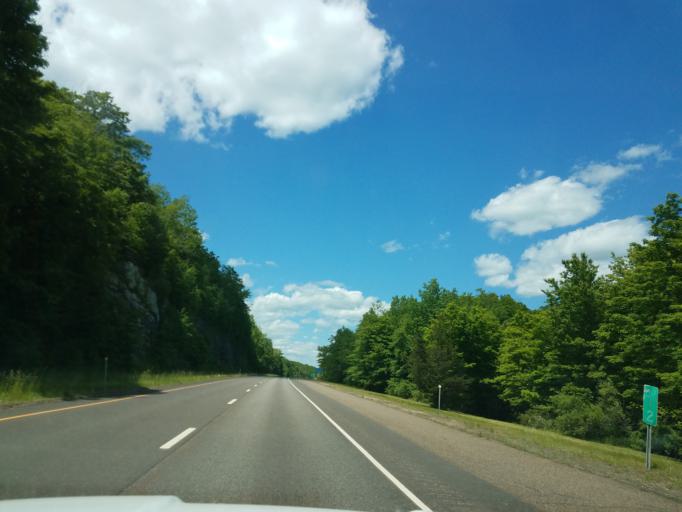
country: US
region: Connecticut
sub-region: New London County
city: Colchester
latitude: 41.4856
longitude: -72.2998
